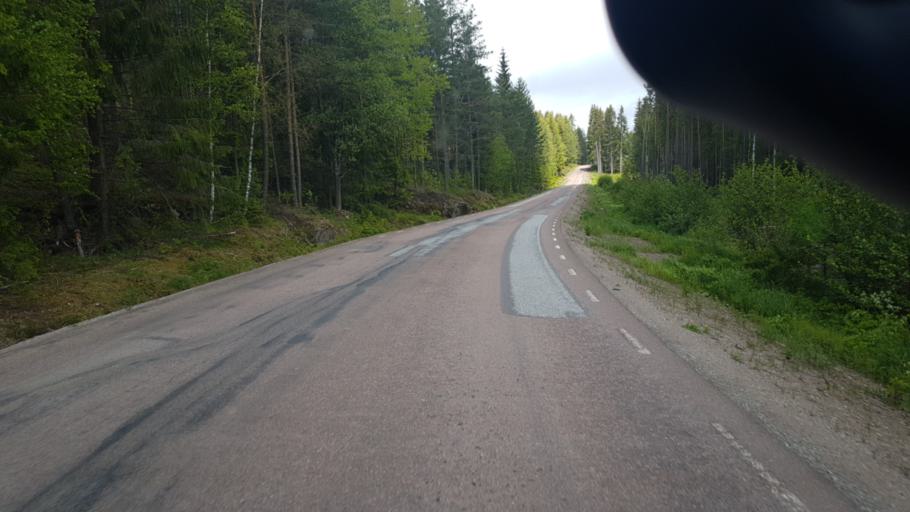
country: SE
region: Vaermland
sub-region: Arvika Kommun
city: Arvika
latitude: 59.6845
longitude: 12.4741
